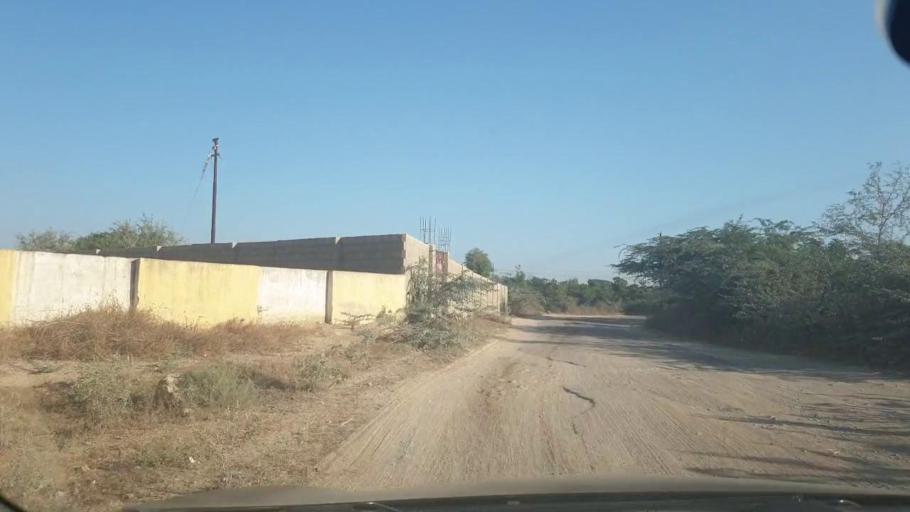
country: PK
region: Sindh
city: Malir Cantonment
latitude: 25.1028
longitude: 67.2573
